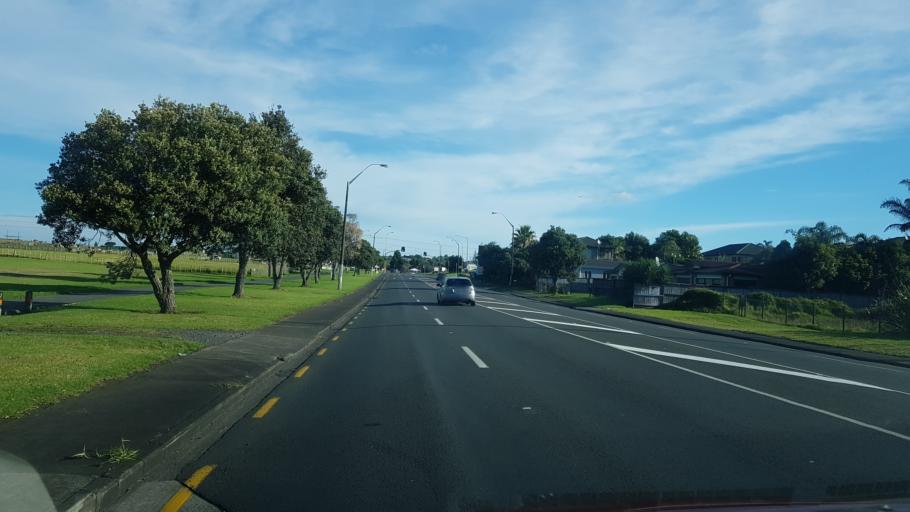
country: NZ
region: Auckland
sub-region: Auckland
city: Rosebank
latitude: -36.8506
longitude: 174.6512
